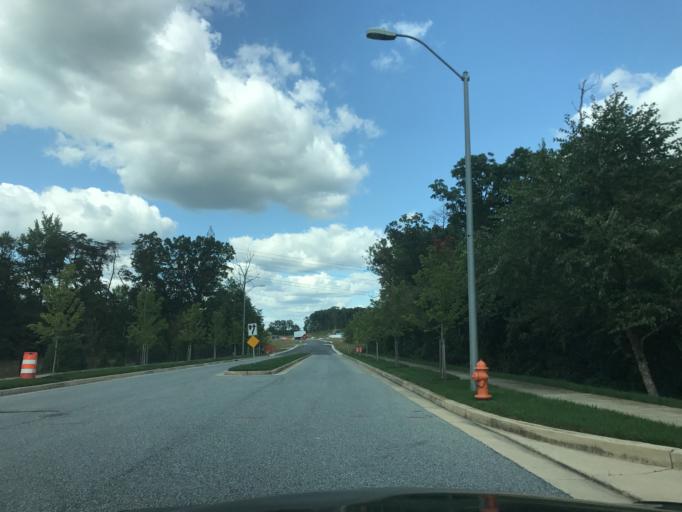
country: US
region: Maryland
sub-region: Baltimore County
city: Bowleys Quarters
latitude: 39.3552
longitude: -76.4029
